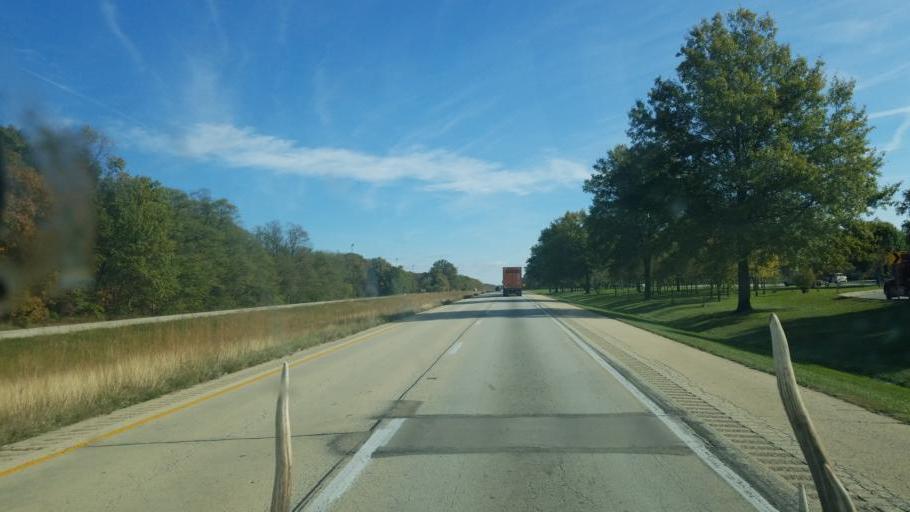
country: US
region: Illinois
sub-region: Effingham County
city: Altamont
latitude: 39.0652
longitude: -88.6766
